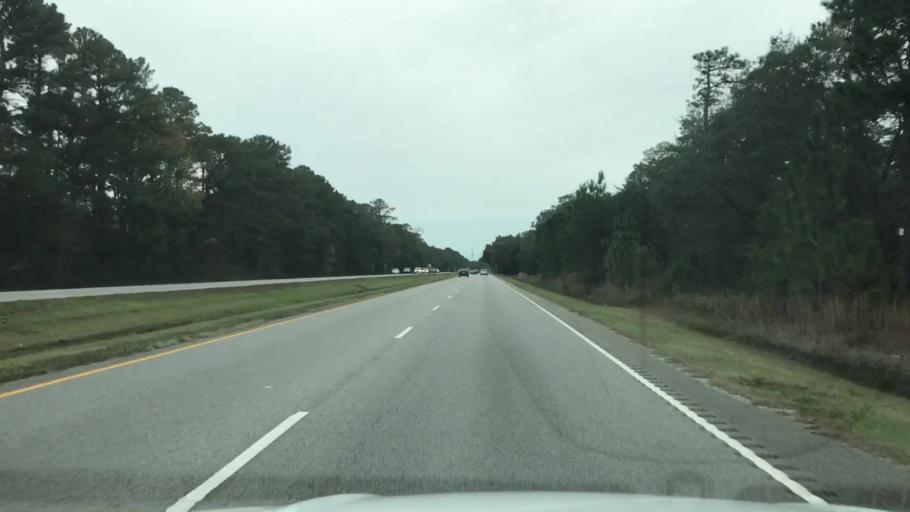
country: US
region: South Carolina
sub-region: Georgetown County
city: Georgetown
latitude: 33.3798
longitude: -79.2101
